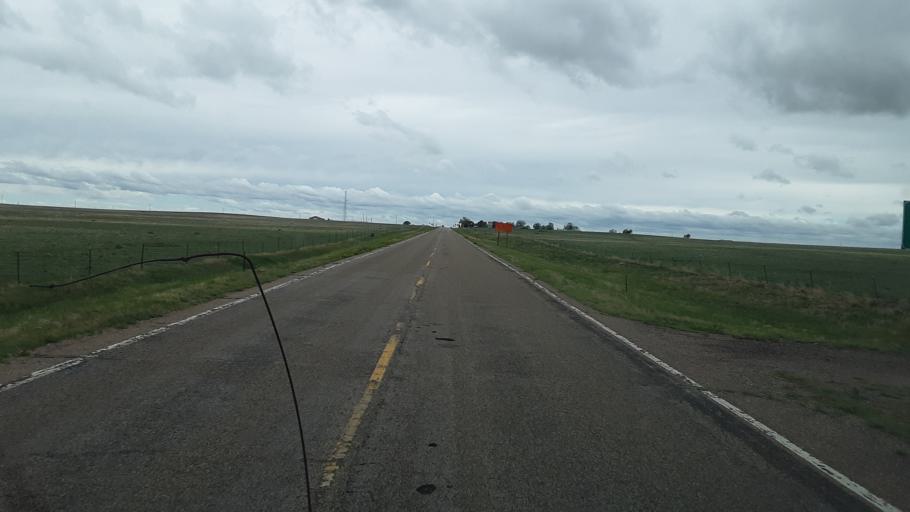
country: US
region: Colorado
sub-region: Lincoln County
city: Hugo
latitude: 38.8519
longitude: -103.6909
